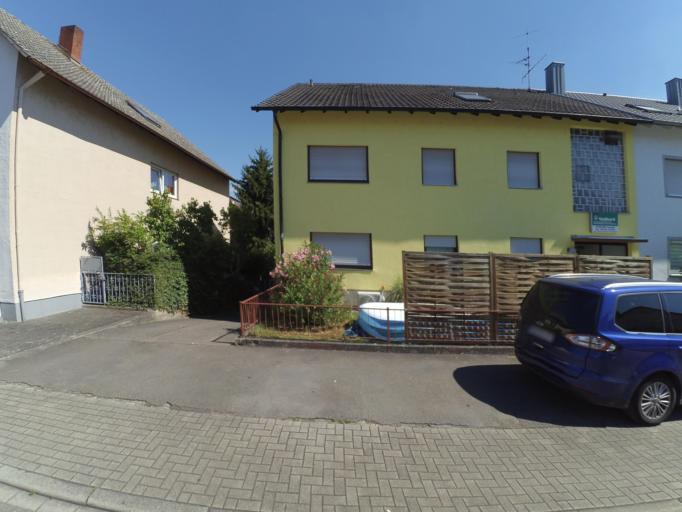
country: DE
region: Baden-Wuerttemberg
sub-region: Karlsruhe Region
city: Bruhl
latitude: 49.4002
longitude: 8.5321
